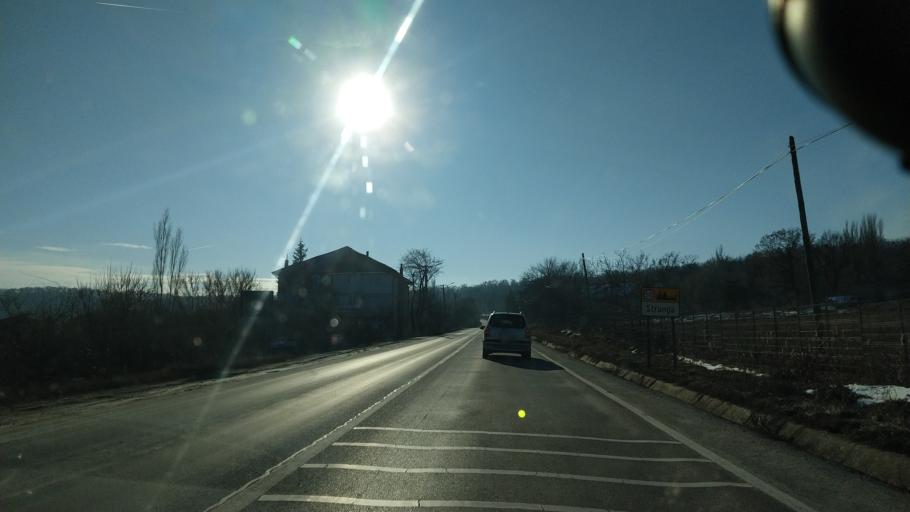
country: RO
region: Iasi
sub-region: Comuna Strunga
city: Strunga
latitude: 47.1702
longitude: 26.9544
